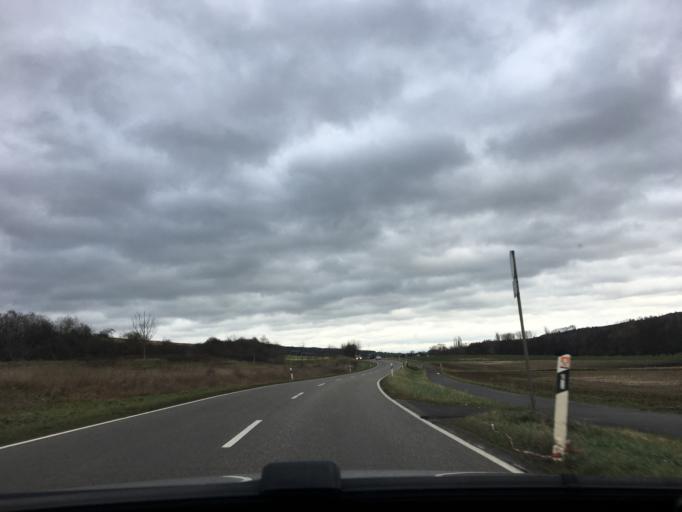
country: DE
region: Rheinland-Pfalz
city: Ebertsheim
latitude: 49.5647
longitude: 8.0928
